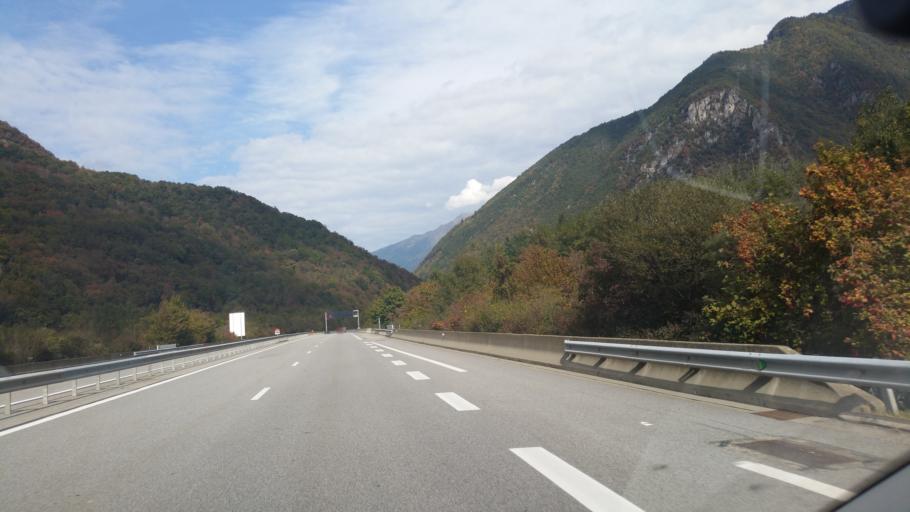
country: FR
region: Rhone-Alpes
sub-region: Departement de la Savoie
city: Saint-Remy-de-Maurienne
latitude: 45.4491
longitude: 6.2862
